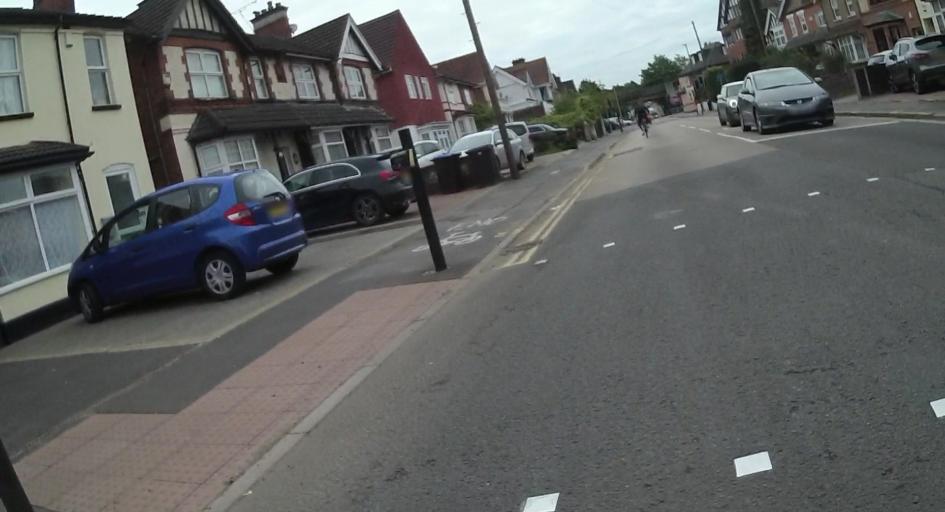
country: GB
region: England
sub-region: Surrey
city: Woking
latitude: 51.3261
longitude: -0.5423
